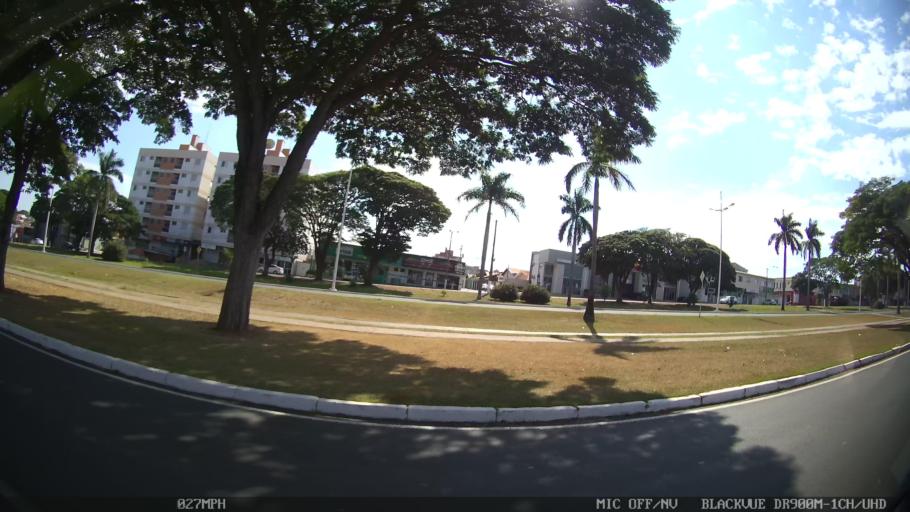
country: BR
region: Sao Paulo
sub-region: Americana
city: Americana
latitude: -22.7331
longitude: -47.3107
